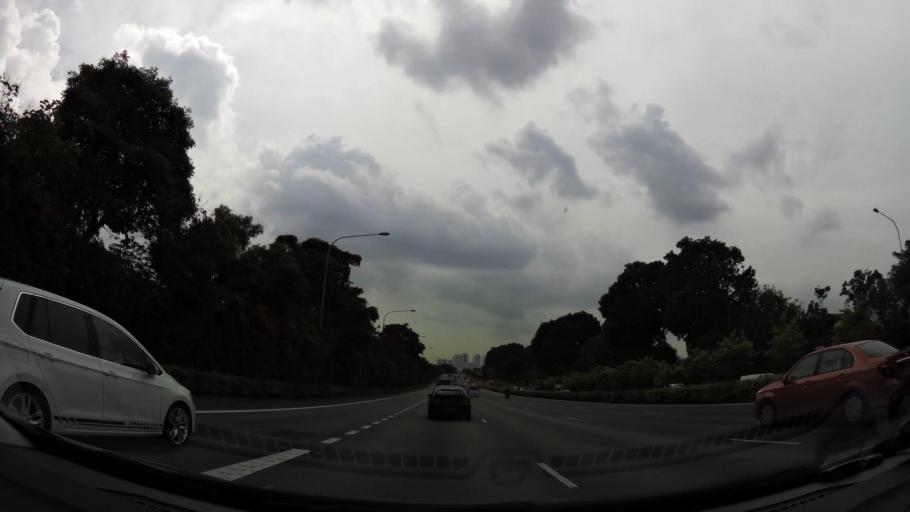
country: MY
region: Johor
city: Kampung Pasir Gudang Baru
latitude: 1.3880
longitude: 103.8584
